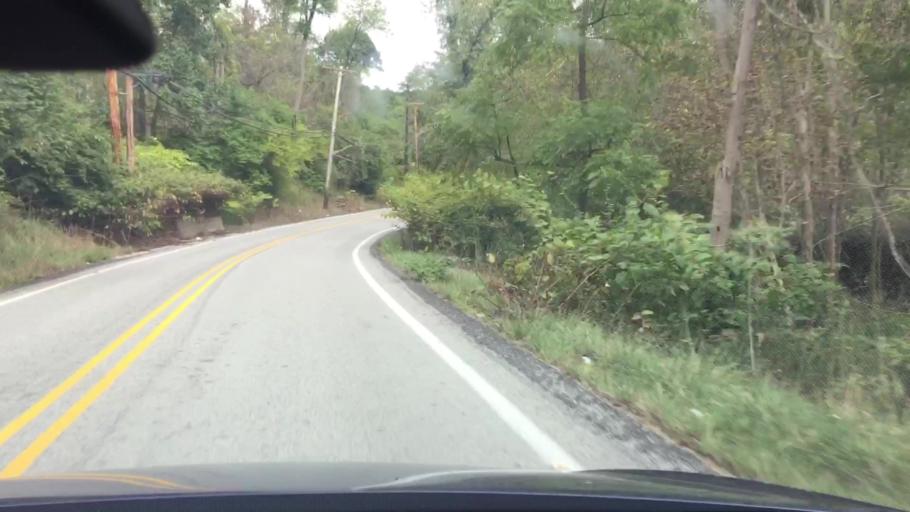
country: US
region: Pennsylvania
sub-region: Allegheny County
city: Penn Hills
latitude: 40.4930
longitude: -79.8107
